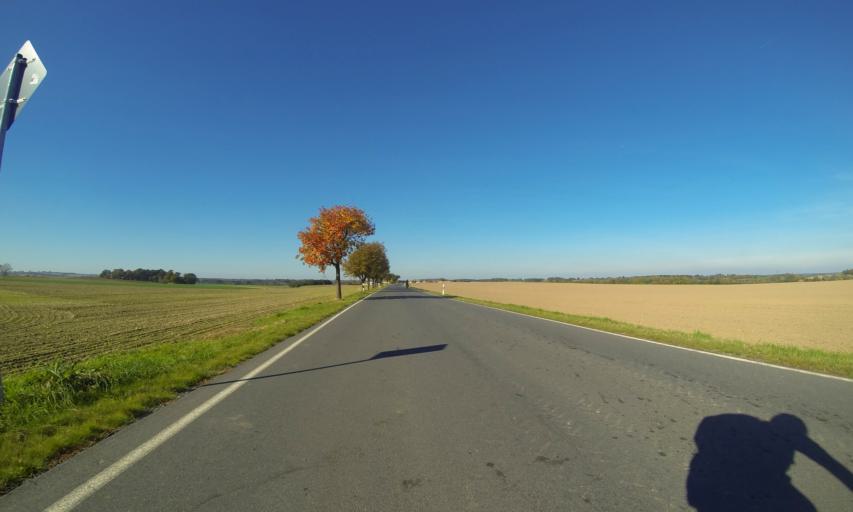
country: DE
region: Saxony
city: Ebersbach
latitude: 51.2420
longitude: 13.5913
